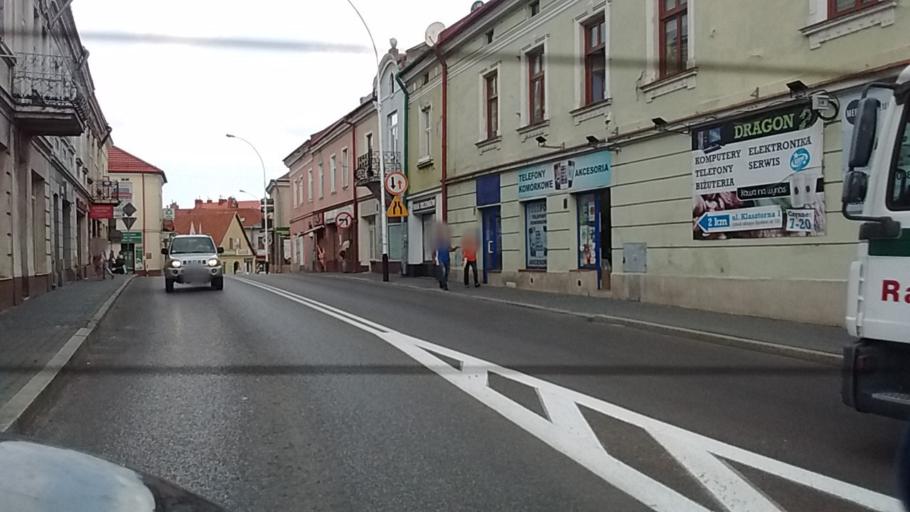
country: PL
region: Subcarpathian Voivodeship
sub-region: Powiat lezajski
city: Lezajsk
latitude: 50.2534
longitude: 22.4228
